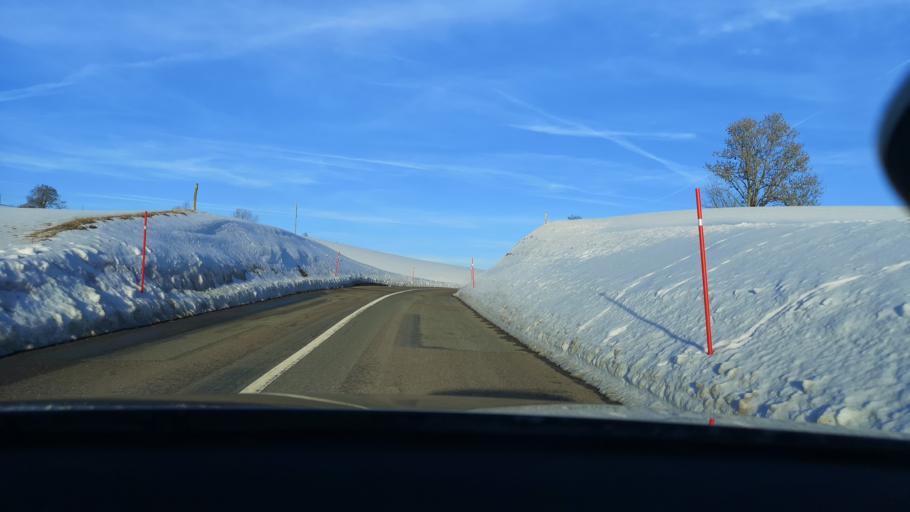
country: CH
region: Neuchatel
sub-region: Val-de-Travers District
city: Fleurier
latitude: 46.9108
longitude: 6.5027
